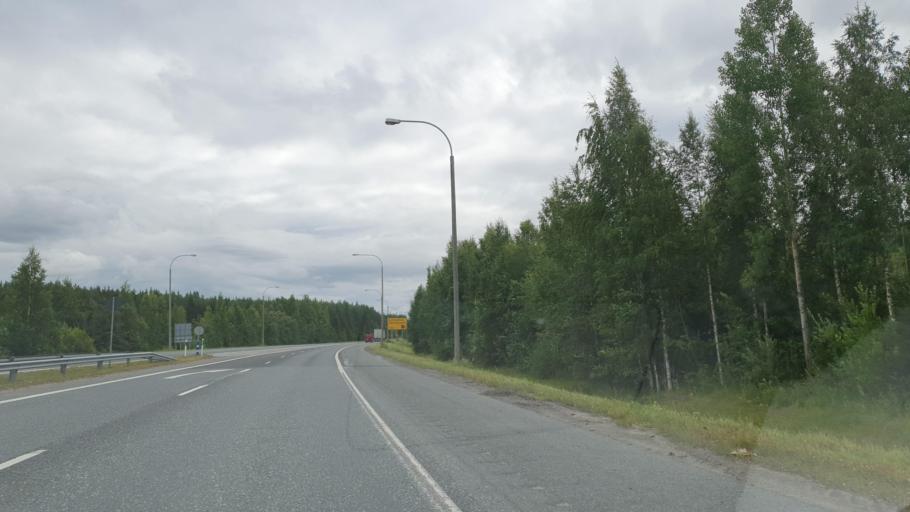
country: FI
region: Northern Savo
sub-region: Ylae-Savo
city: Iisalmi
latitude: 63.5167
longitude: 27.2567
